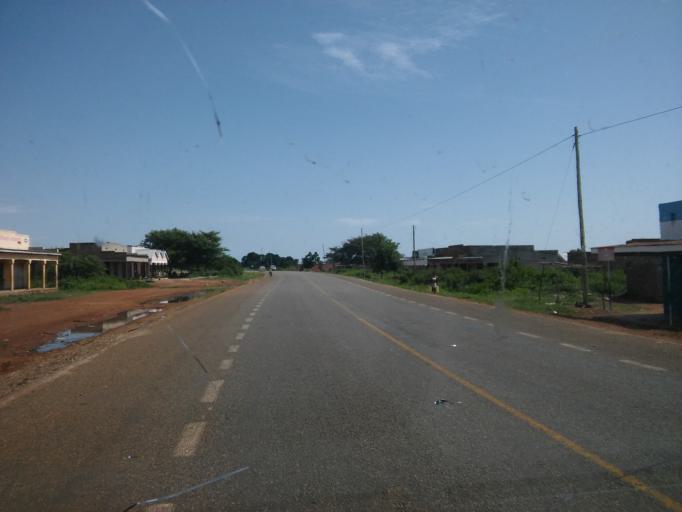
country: UG
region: Eastern Region
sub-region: Bukedea District
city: Bukedea
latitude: 1.3511
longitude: 34.0405
